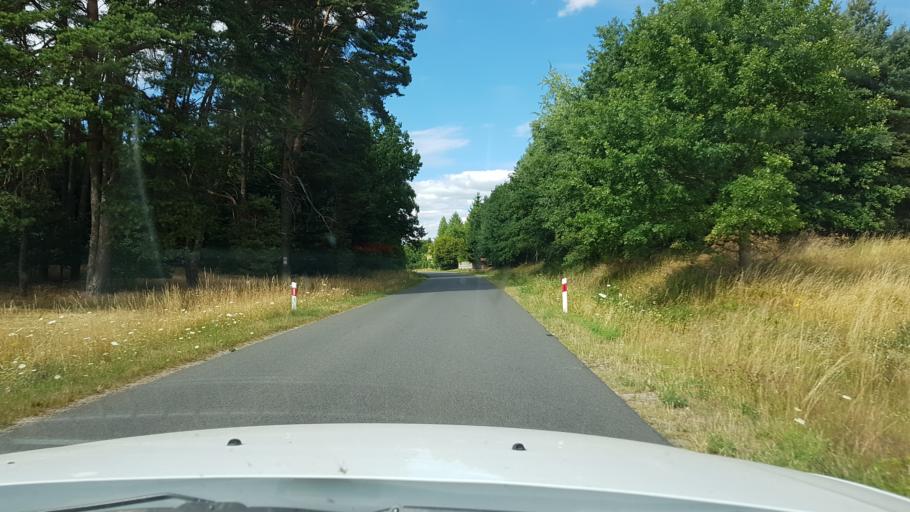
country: PL
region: West Pomeranian Voivodeship
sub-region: Powiat drawski
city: Kalisz Pomorski
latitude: 53.3654
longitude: 15.9354
